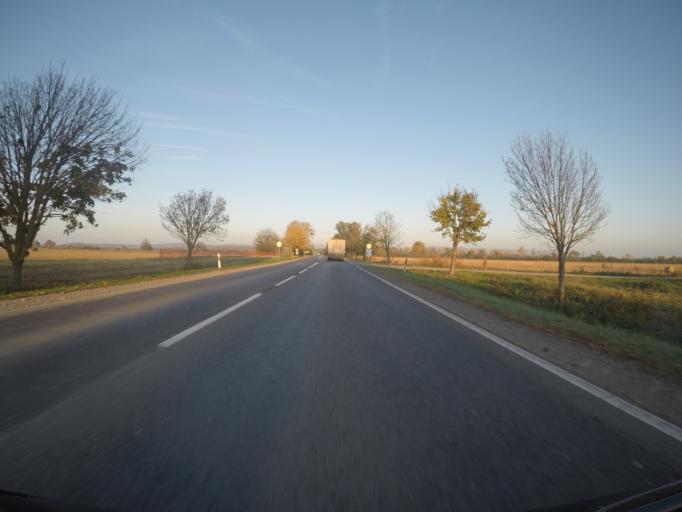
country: HU
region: Baranya
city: Szentlorinc
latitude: 46.0405
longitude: 17.9663
